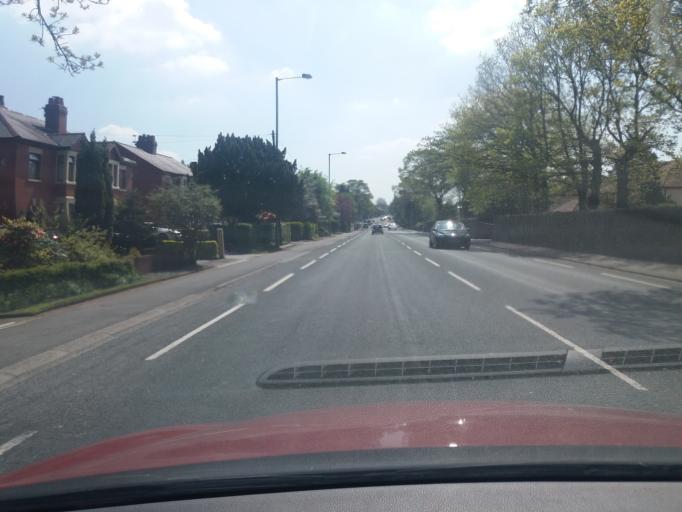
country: GB
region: England
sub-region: Lancashire
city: Clayton-le-Woods
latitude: 53.6799
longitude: -2.6366
